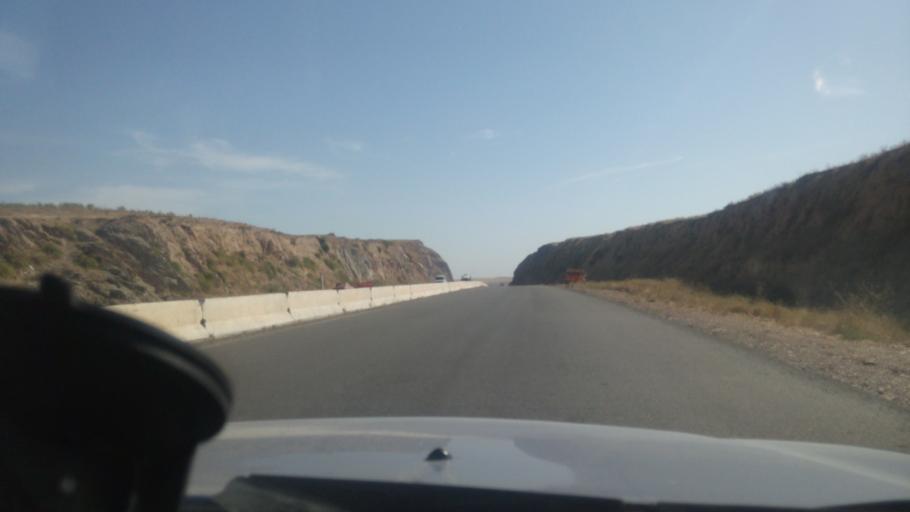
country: UZ
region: Jizzax
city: Jizzax
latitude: 40.0471
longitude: 67.6754
